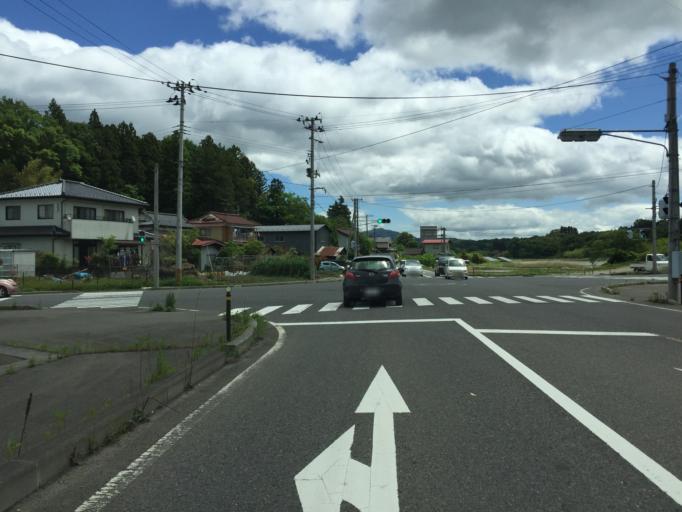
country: JP
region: Fukushima
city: Motomiya
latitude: 37.5196
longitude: 140.4579
